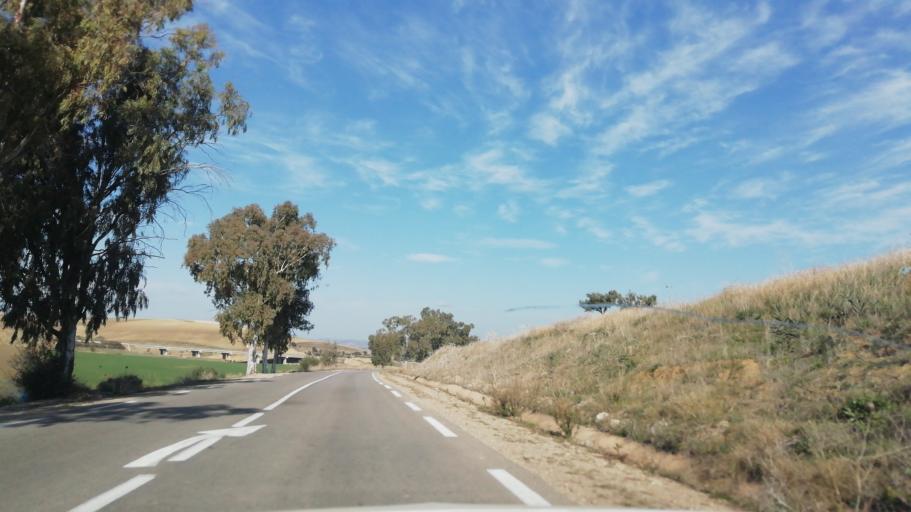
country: DZ
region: Tlemcen
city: Chetouane
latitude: 34.9733
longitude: -1.2441
